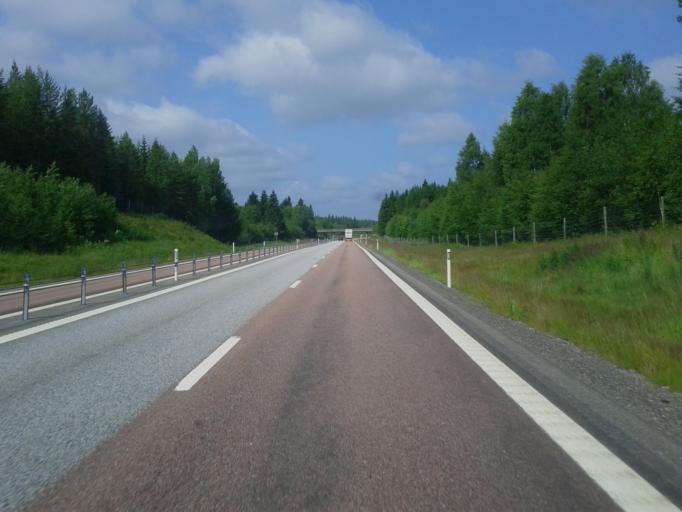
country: SE
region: Vaesterbotten
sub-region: Skelleftea Kommun
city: Soedra Bergsbyn
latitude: 64.6946
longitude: 21.0225
